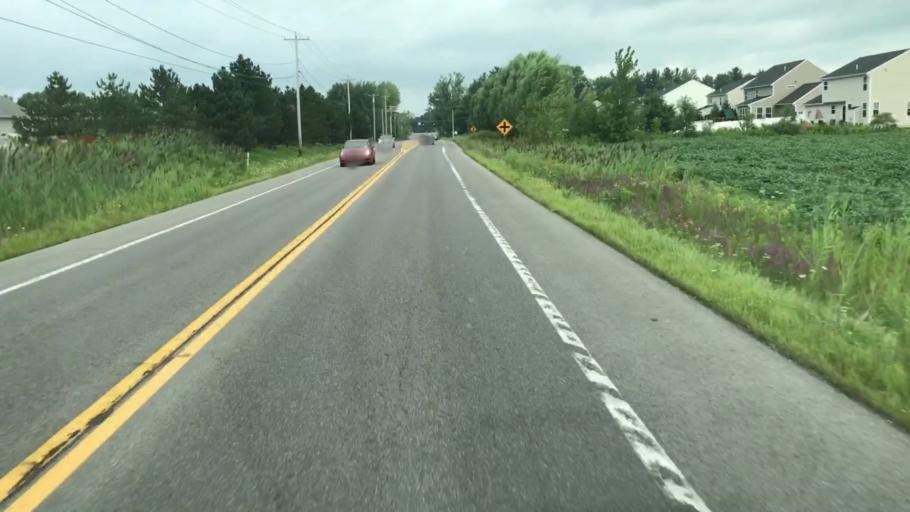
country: US
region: New York
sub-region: Onondaga County
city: Liverpool
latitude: 43.1659
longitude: -76.2087
